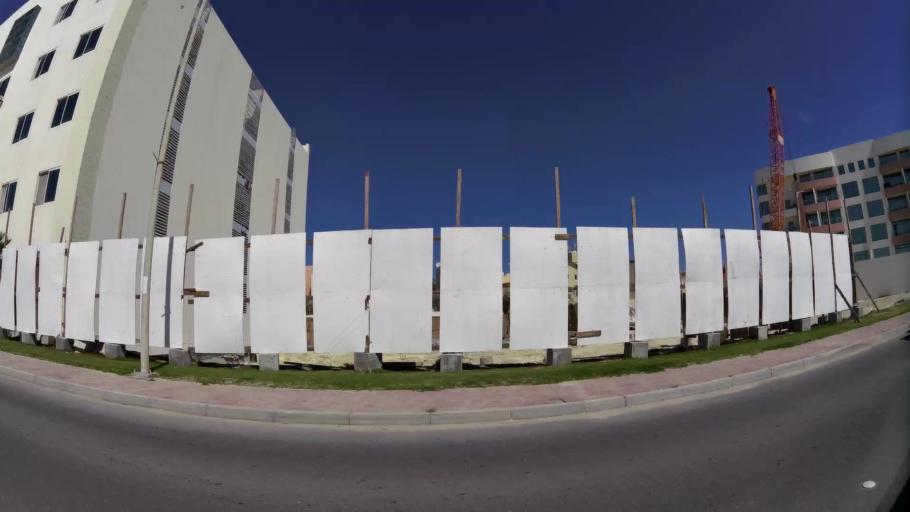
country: BH
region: Muharraq
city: Al Hadd
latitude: 26.2951
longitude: 50.6586
